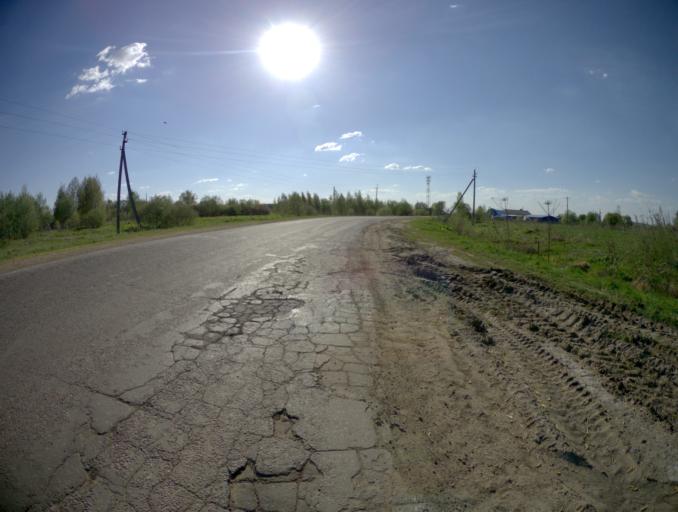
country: RU
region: Ivanovo
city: Gavrilov Posad
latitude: 56.3445
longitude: 40.1902
